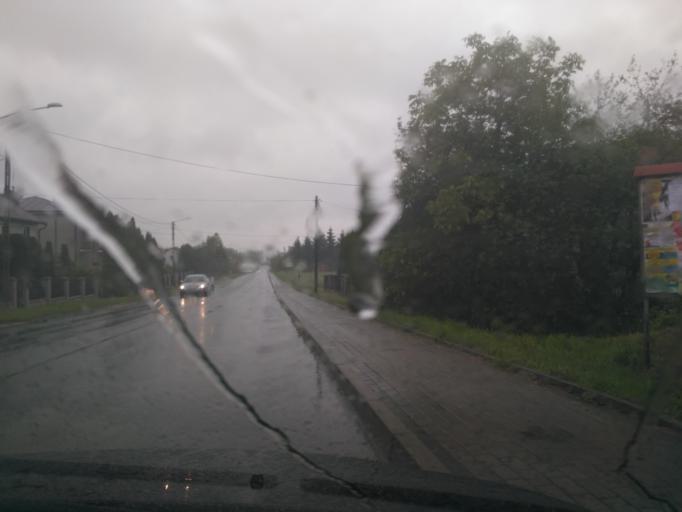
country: PL
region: Subcarpathian Voivodeship
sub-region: Powiat jasielski
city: Jaslo
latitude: 49.7340
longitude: 21.4727
